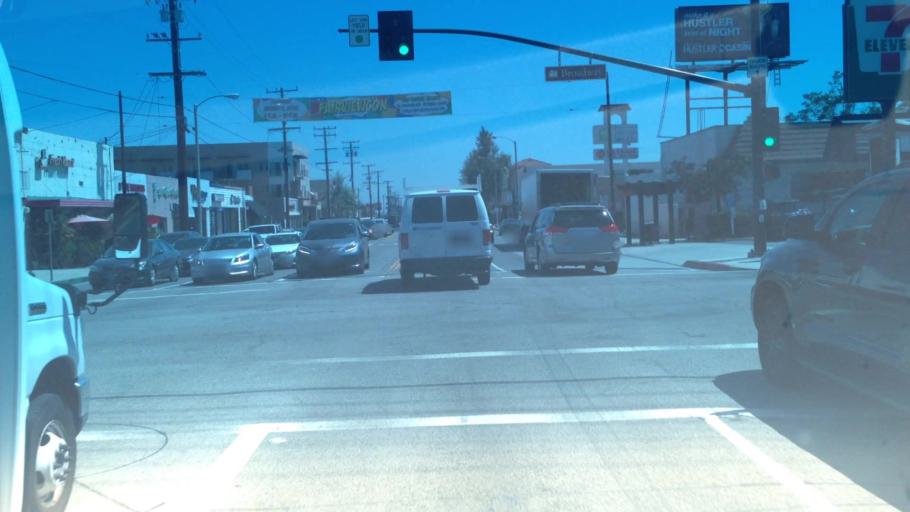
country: US
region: California
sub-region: Los Angeles County
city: East San Gabriel
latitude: 34.0992
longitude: -118.0911
